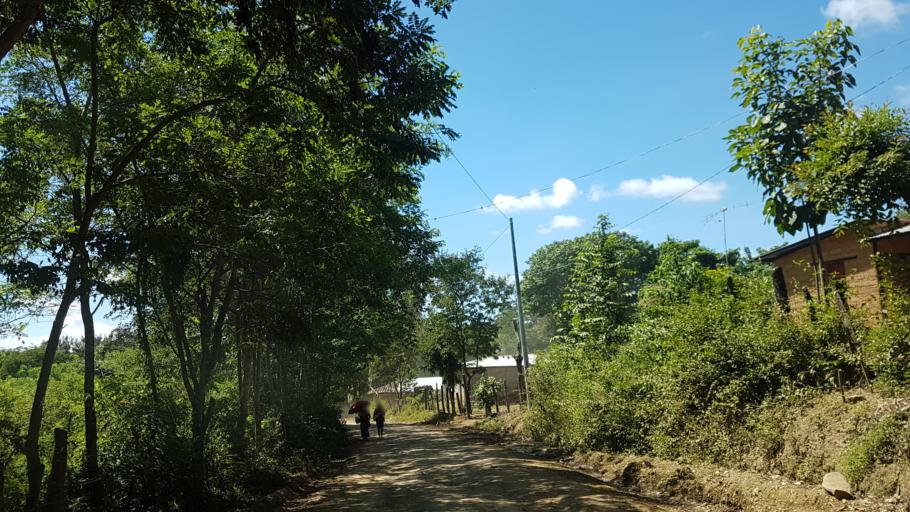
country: HN
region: El Paraiso
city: Santa Cruz
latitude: 13.7328
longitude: -86.6800
